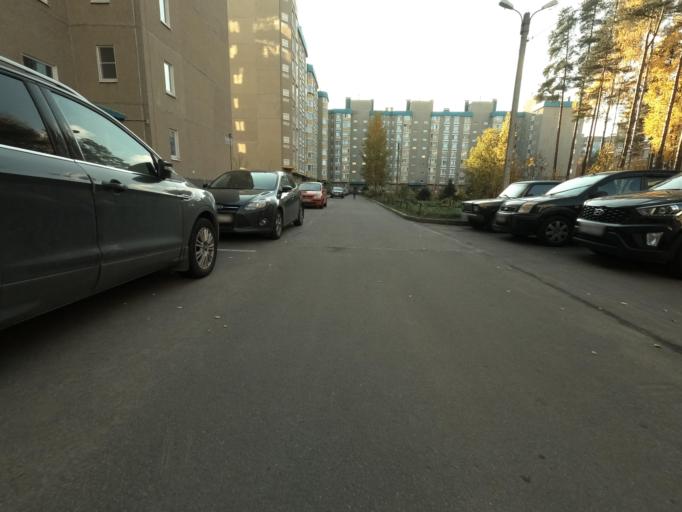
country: RU
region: Leningrad
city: Sertolovo
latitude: 60.1433
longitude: 30.2303
